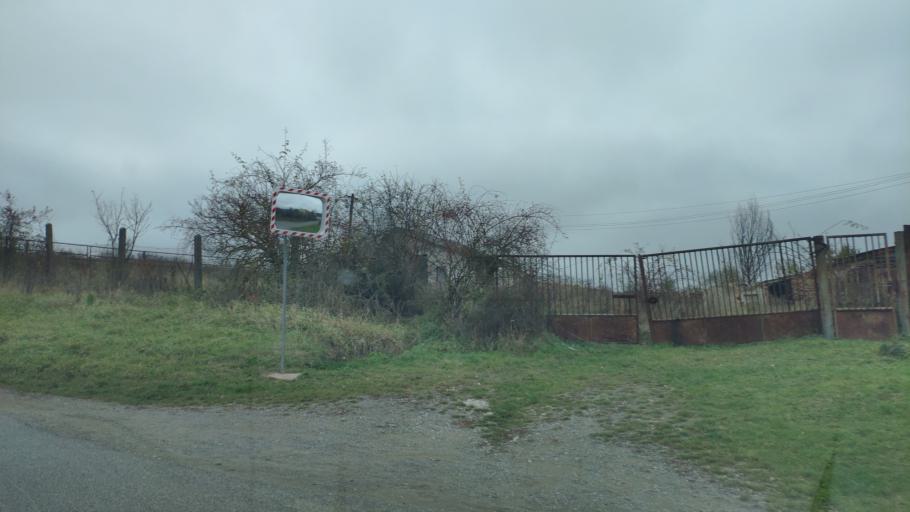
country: SK
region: Presovsky
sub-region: Okres Presov
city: Presov
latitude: 49.1203
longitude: 21.2527
